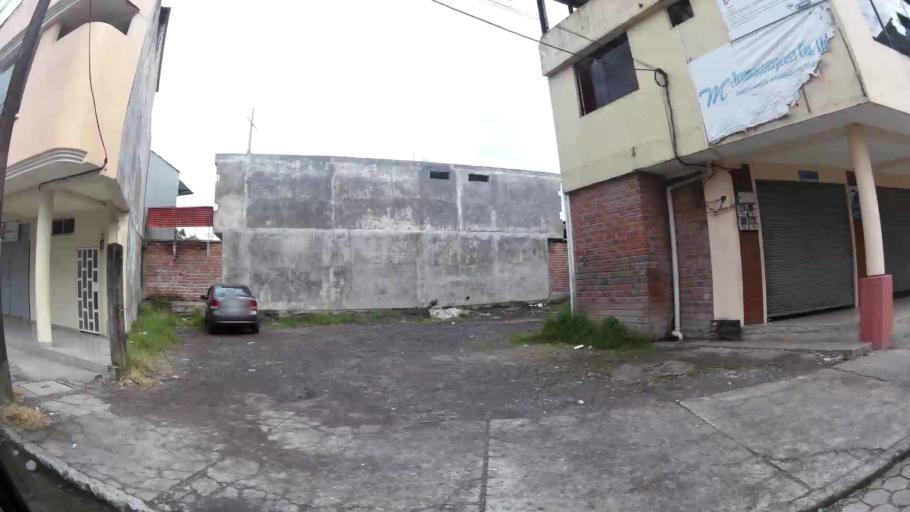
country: EC
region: Pastaza
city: Puyo
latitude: -1.4849
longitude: -78.0005
